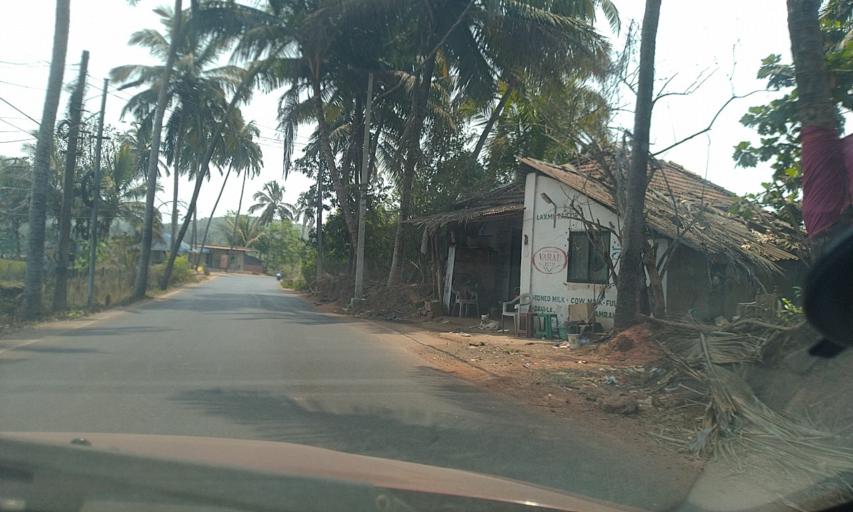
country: IN
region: Goa
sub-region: North Goa
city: Vagator
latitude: 15.5920
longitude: 73.7627
